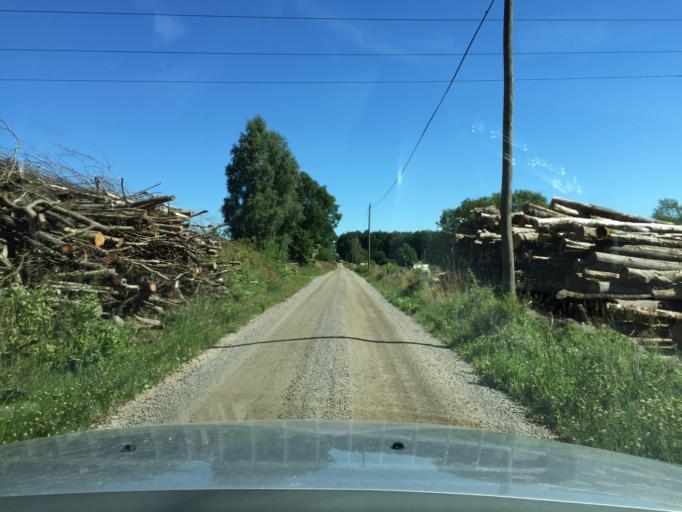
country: SE
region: Skane
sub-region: Hassleholms Kommun
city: Sosdala
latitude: 56.0145
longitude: 13.6344
